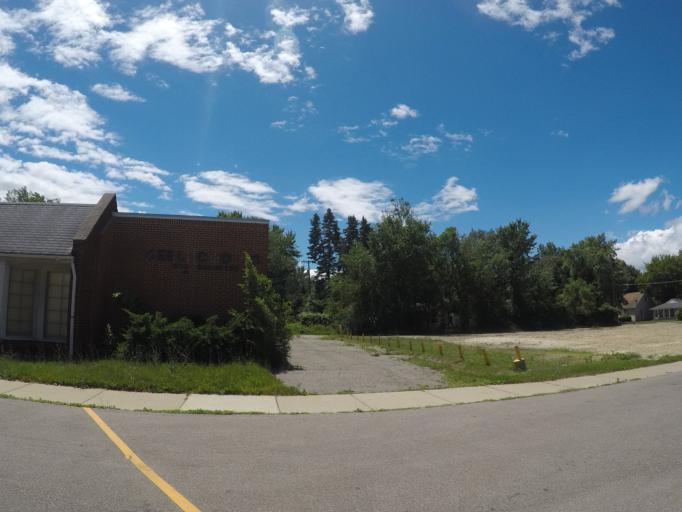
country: US
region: Michigan
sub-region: Wayne County
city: Redford
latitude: 42.4283
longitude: -83.2950
